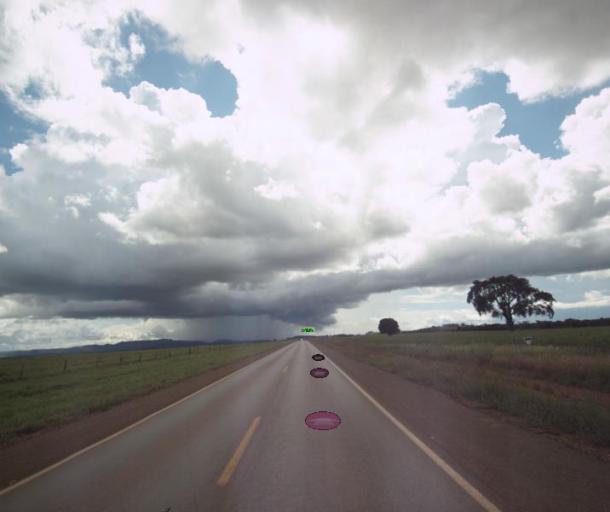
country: BR
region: Goias
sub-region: Uruacu
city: Uruacu
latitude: -14.6947
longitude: -49.1163
